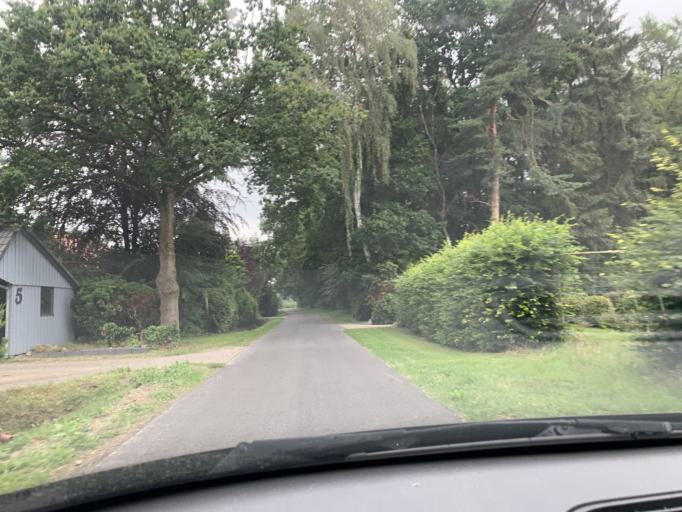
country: DE
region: Lower Saxony
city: Westerstede
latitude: 53.2510
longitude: 7.9803
